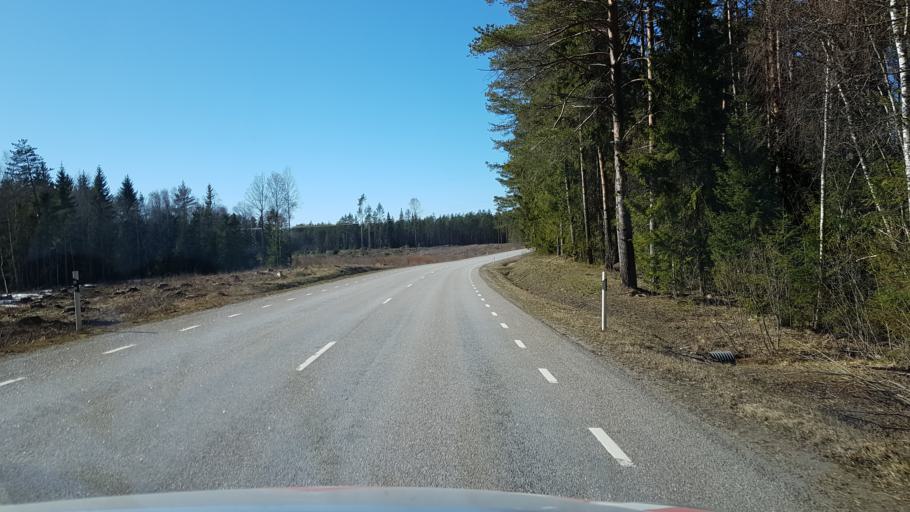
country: EE
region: Laeaene-Virumaa
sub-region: Viru-Nigula vald
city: Kunda
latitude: 59.3677
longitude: 26.6009
